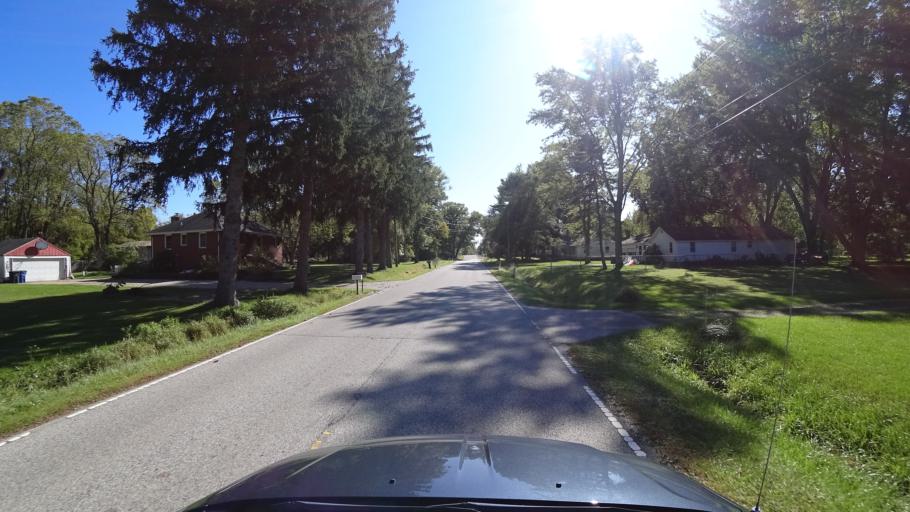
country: US
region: Indiana
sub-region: LaPorte County
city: Long Beach
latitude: 41.7392
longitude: -86.8162
